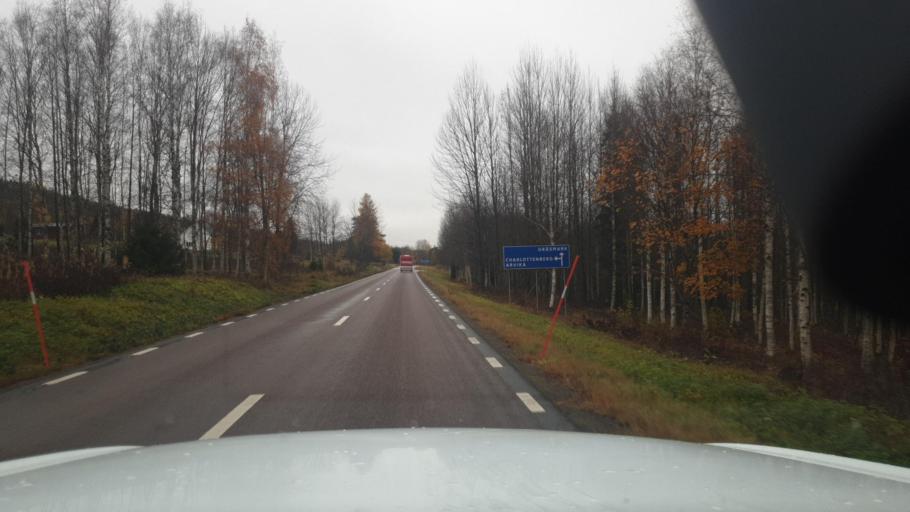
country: SE
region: Vaermland
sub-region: Torsby Kommun
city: Torsby
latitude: 59.9232
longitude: 12.8976
